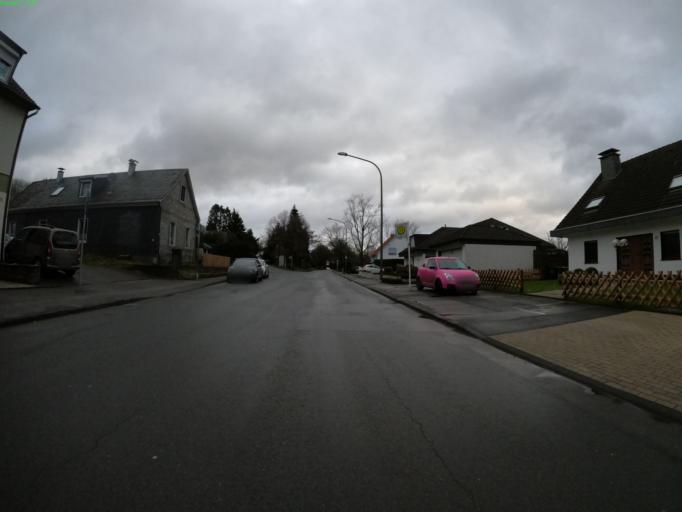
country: DE
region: North Rhine-Westphalia
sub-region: Regierungsbezirk Dusseldorf
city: Remscheid
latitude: 51.1808
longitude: 7.1395
